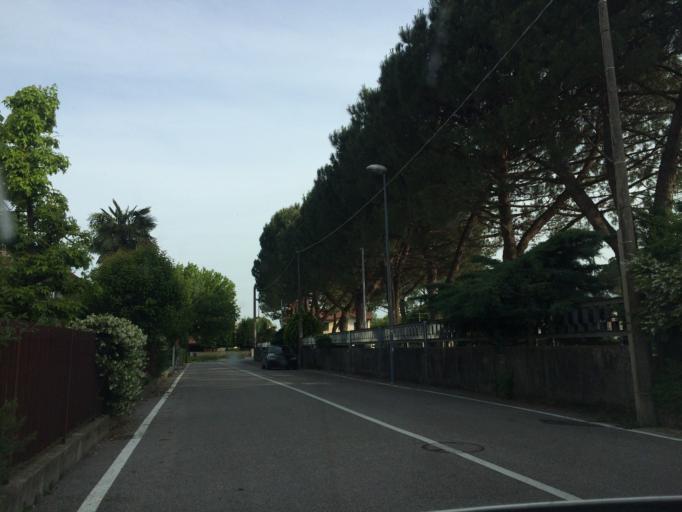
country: IT
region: Veneto
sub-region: Provincia di Padova
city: Cittadella
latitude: 45.6388
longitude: 11.7804
